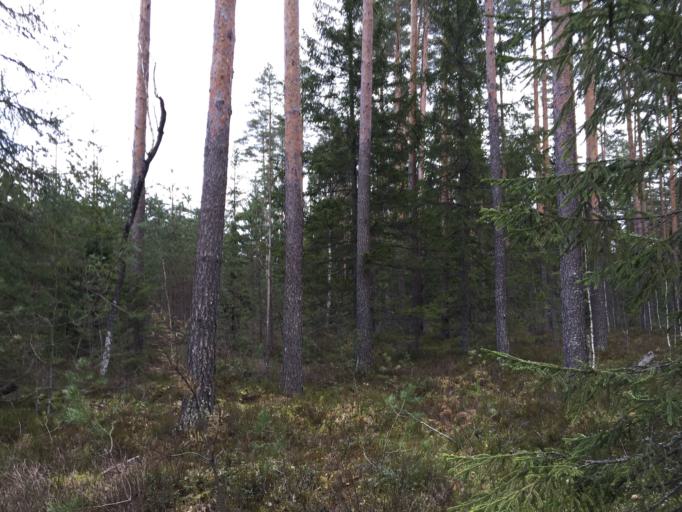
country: LV
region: Garkalne
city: Garkalne
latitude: 56.9620
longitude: 24.4834
